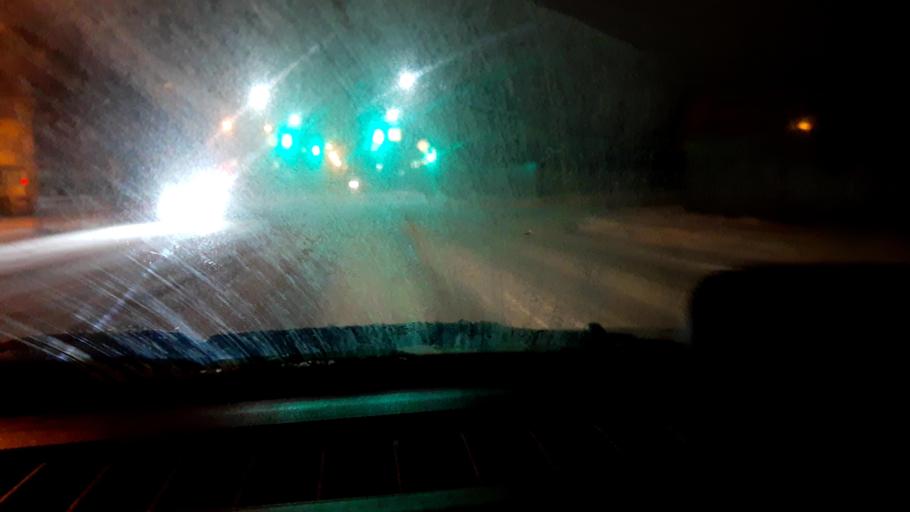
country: RU
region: Nizjnij Novgorod
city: Kstovo
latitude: 56.1434
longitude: 44.1811
